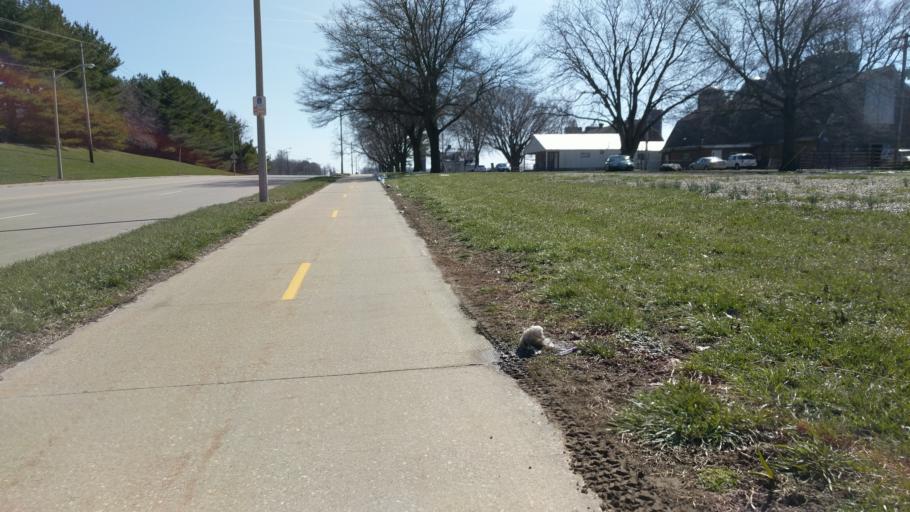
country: US
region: Illinois
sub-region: Champaign County
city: Urbana
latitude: 40.0906
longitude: -88.2191
